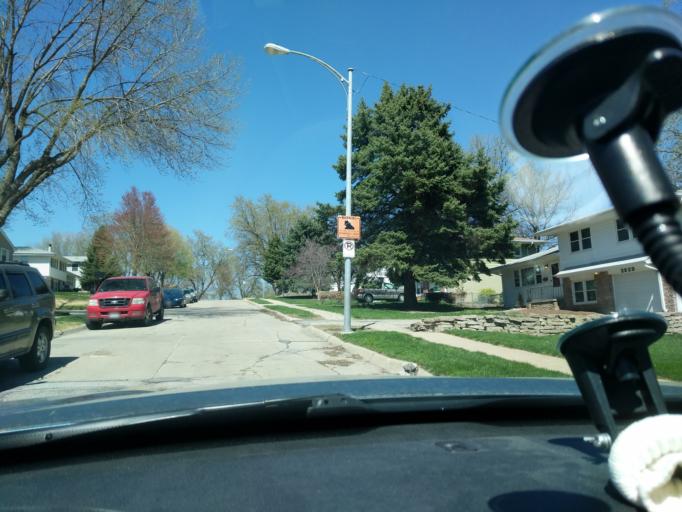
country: US
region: Nebraska
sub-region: Douglas County
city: Ralston
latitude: 41.2313
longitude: -96.0971
